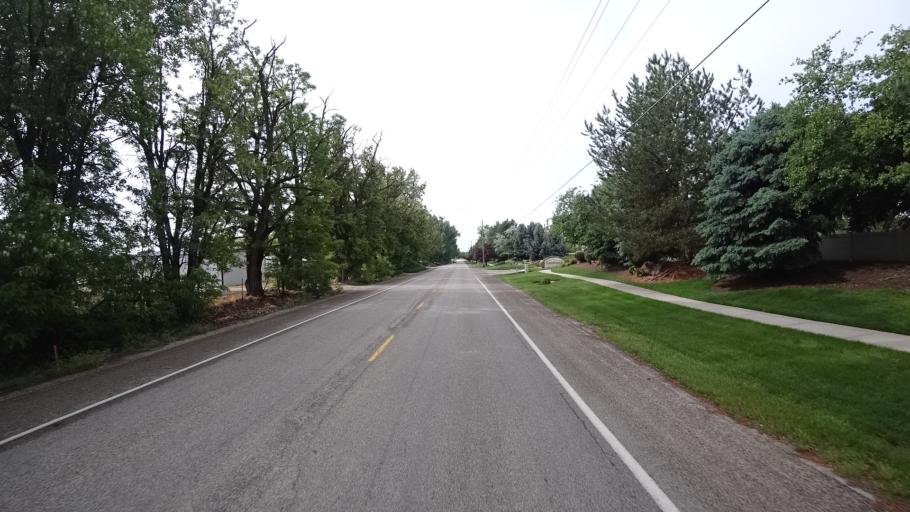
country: US
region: Idaho
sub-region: Ada County
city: Eagle
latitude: 43.7020
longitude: -116.3791
